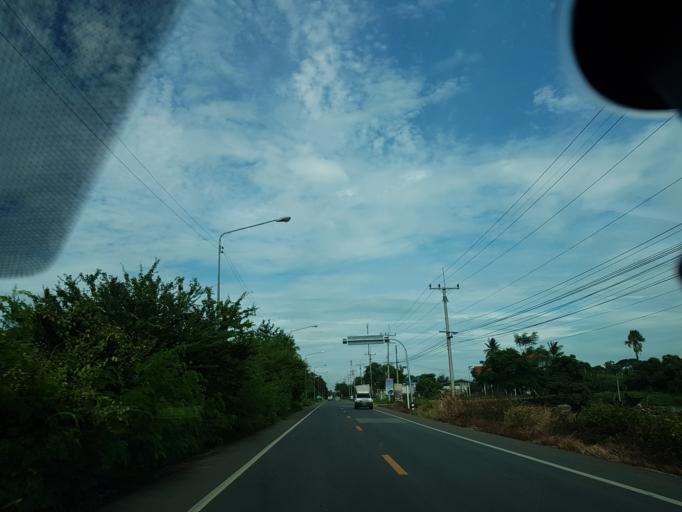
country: TH
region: Lop Buri
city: Tha Wung
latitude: 14.7420
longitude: 100.5409
